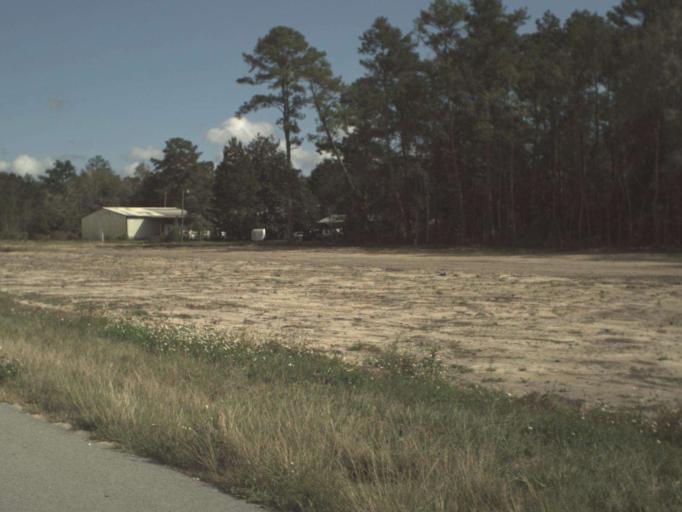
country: US
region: Florida
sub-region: Walton County
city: DeFuniak Springs
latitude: 30.6337
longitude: -86.1159
